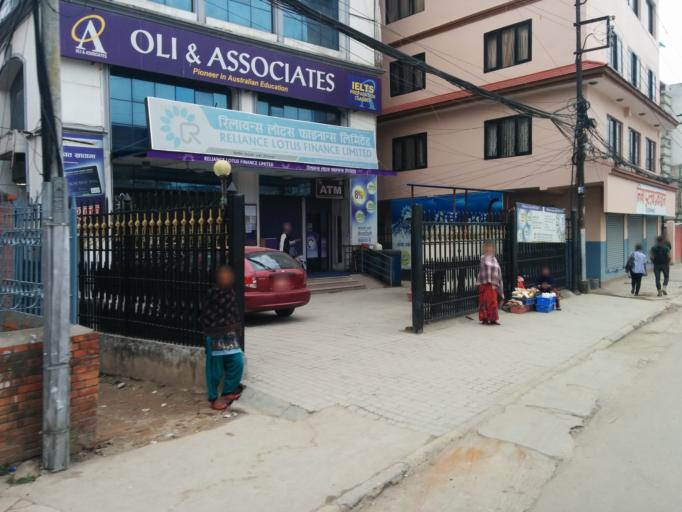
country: NP
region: Central Region
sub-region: Bagmati Zone
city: Kathmandu
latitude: 27.7018
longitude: 85.3212
